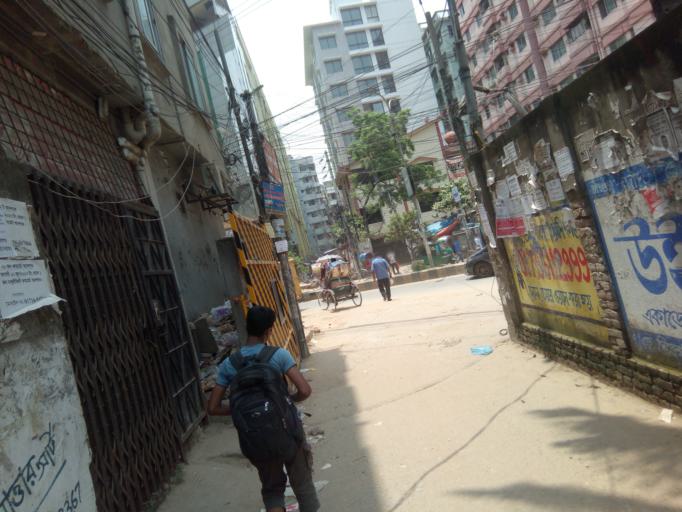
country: BD
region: Dhaka
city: Paltan
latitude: 23.7394
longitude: 90.4149
